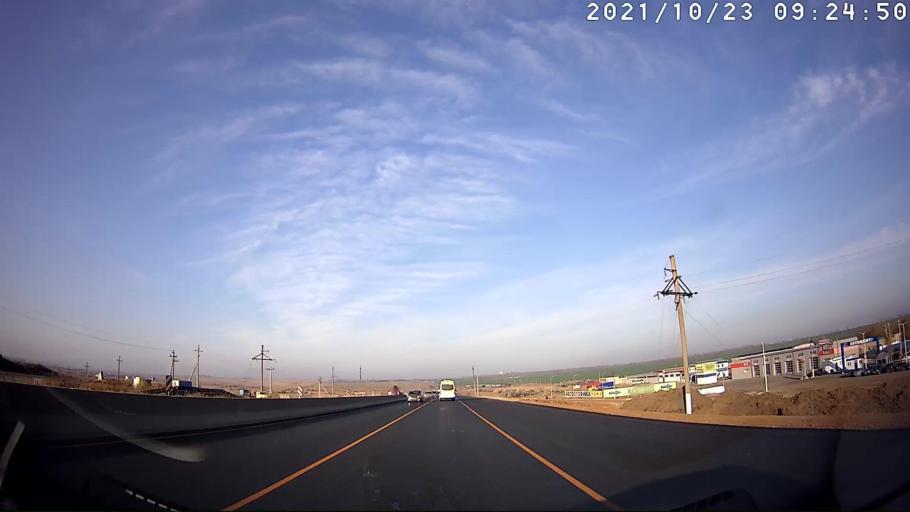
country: RU
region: Saratov
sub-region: Saratovskiy Rayon
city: Saratov
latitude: 51.6708
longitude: 45.9822
